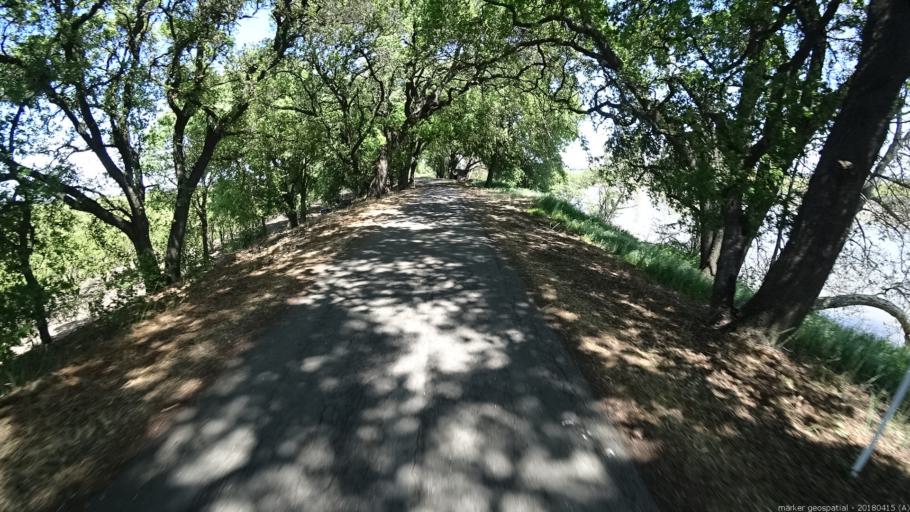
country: US
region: California
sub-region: Sacramento County
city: Walnut Grove
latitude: 38.2781
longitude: -121.5905
